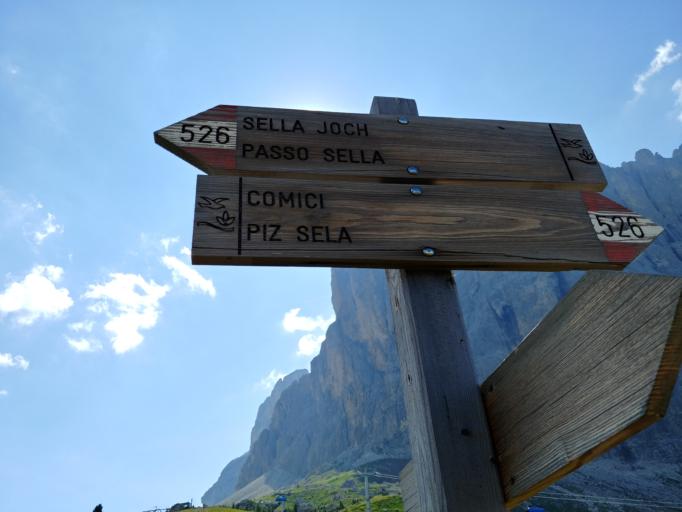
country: IT
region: Trentino-Alto Adige
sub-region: Bolzano
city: Selva
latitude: 46.5188
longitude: 11.7545
